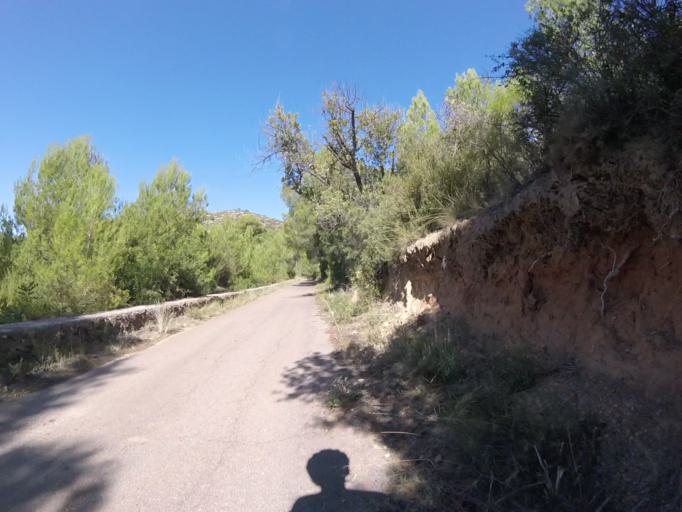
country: ES
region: Valencia
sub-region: Provincia de Castello
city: Cabanes
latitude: 40.1395
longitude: 0.1023
